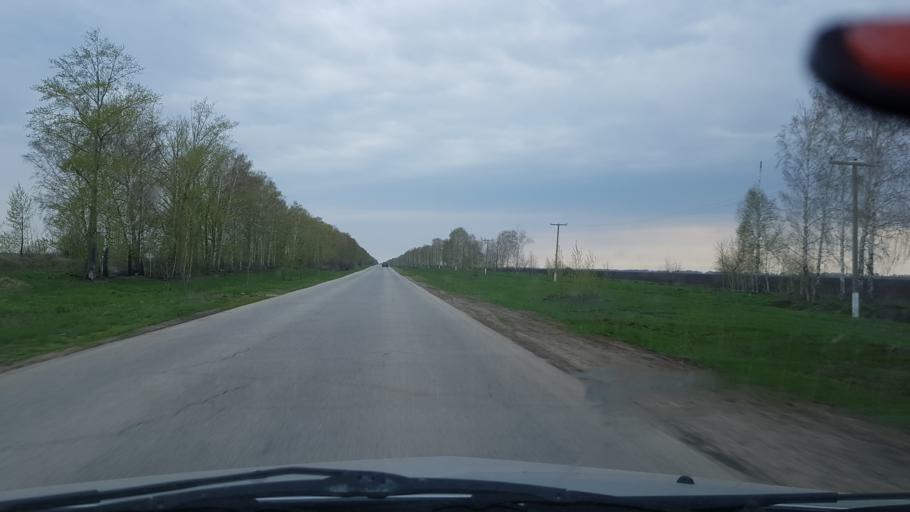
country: RU
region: Samara
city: Tol'yatti
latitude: 53.6585
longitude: 49.2395
